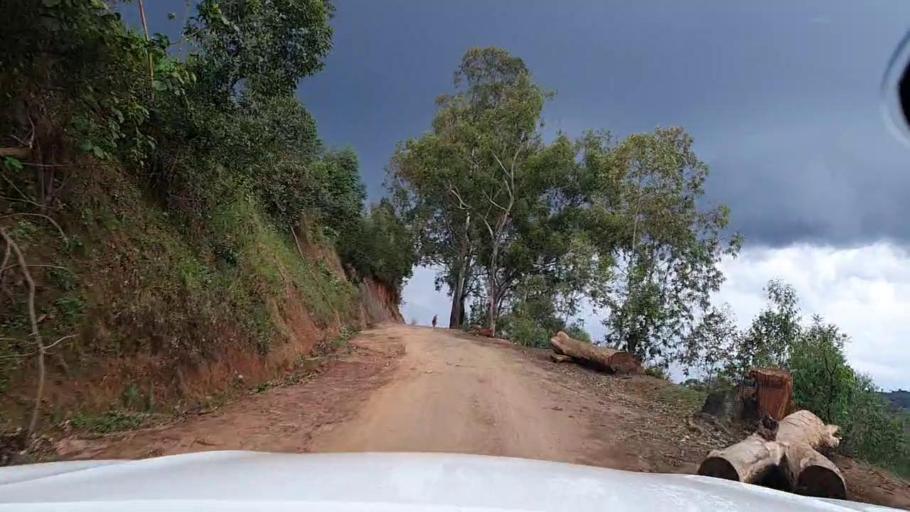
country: BI
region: Kayanza
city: Kayanza
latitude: -2.7911
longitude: 29.5240
